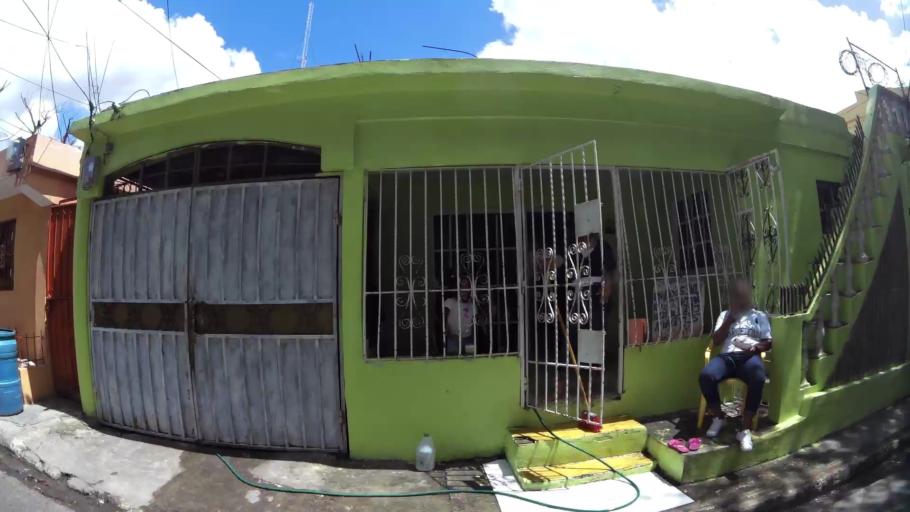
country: DO
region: Nacional
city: Ensanche Luperon
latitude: 18.5222
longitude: -69.9150
